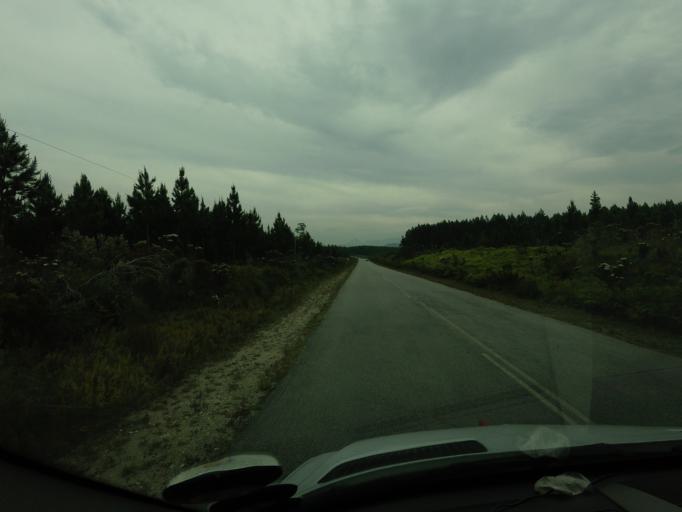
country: ZA
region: Eastern Cape
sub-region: Cacadu District Municipality
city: Kareedouw
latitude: -33.9998
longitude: 23.8566
